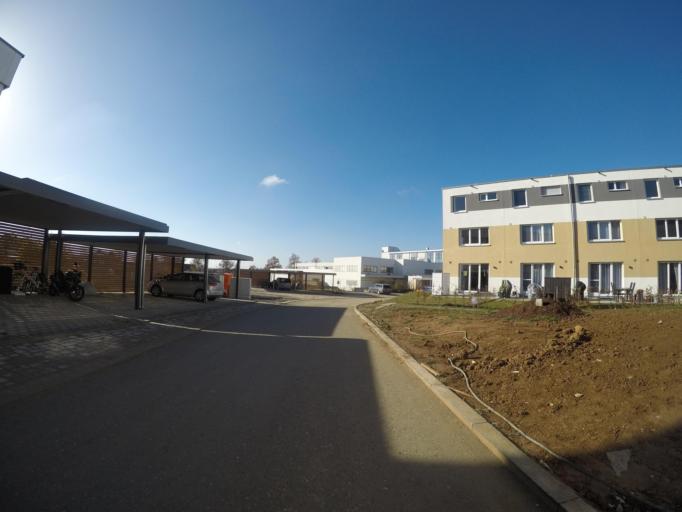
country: DE
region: Baden-Wuerttemberg
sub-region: Tuebingen Region
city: Dornstadt
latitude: 48.4722
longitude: 9.9387
